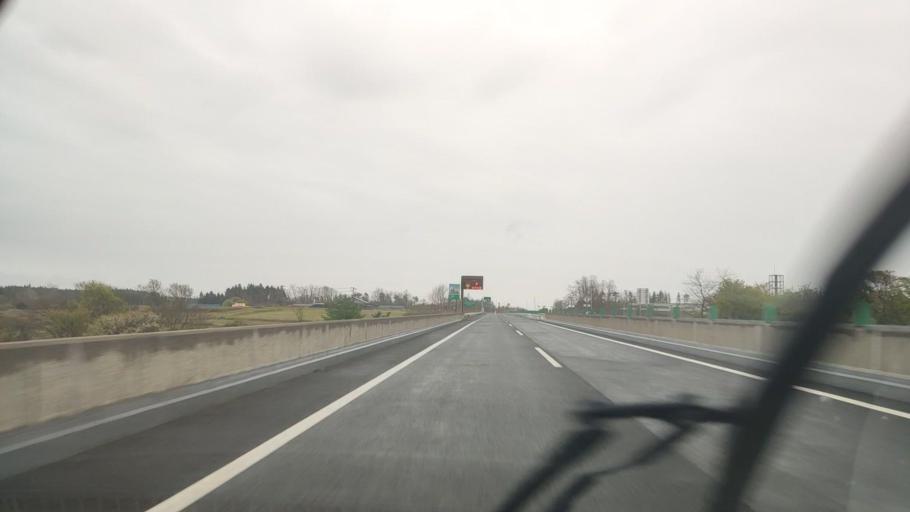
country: JP
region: Akita
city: Noshiromachi
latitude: 40.1253
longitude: 140.0124
